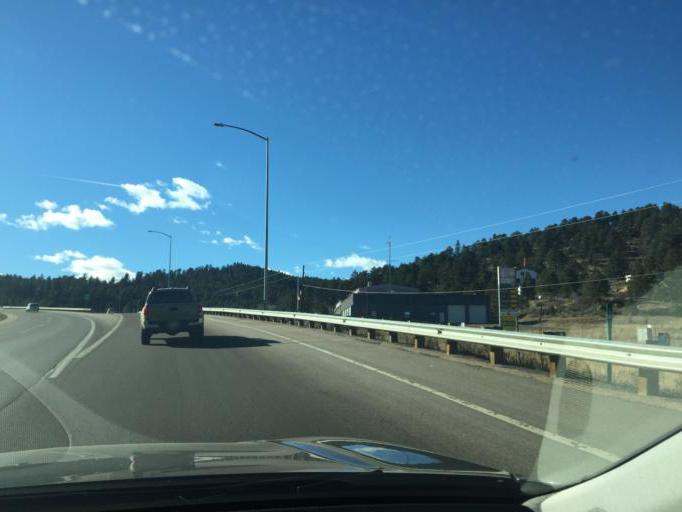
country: US
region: Colorado
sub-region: Jefferson County
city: Evergreen
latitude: 39.4371
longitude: -105.4588
